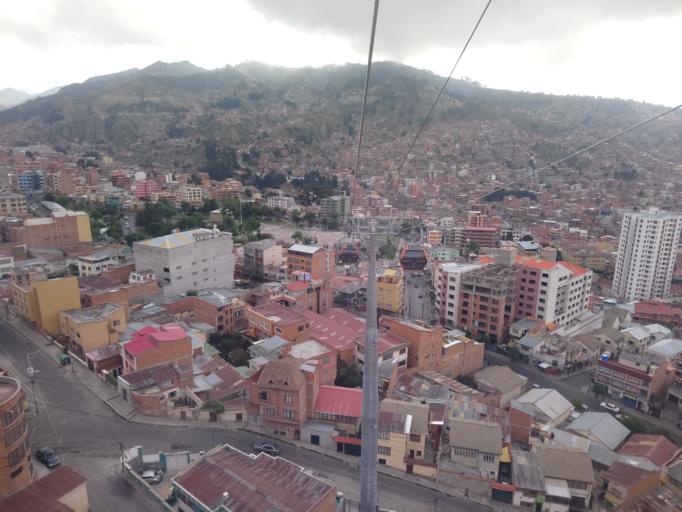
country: BO
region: La Paz
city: La Paz
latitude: -16.4852
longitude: -68.1249
